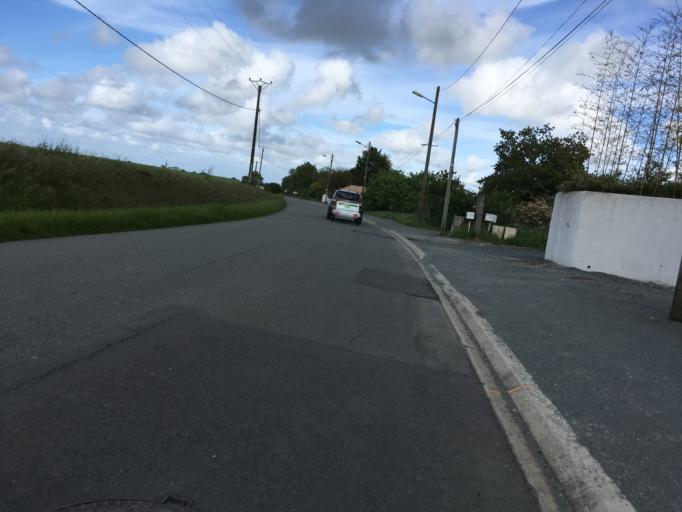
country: FR
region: Poitou-Charentes
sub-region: Departement de la Charente-Maritime
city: Bourgneuf
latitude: 46.1718
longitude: -1.0025
